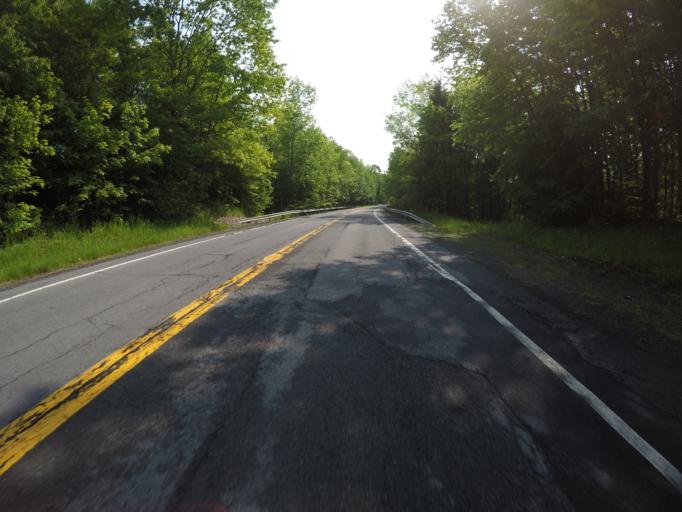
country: US
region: New York
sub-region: Sullivan County
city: Livingston Manor
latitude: 42.1029
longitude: -74.7911
